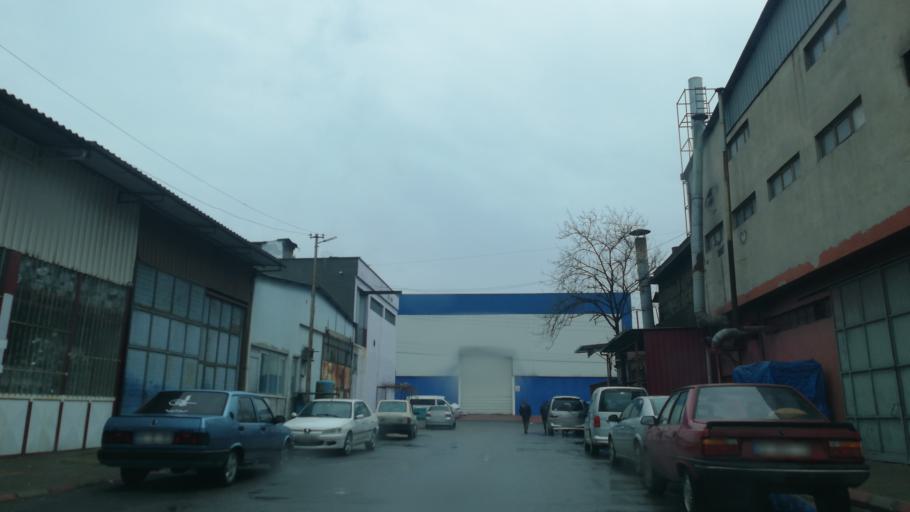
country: TR
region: Kahramanmaras
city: Kahramanmaras
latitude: 37.5597
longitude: 36.9613
